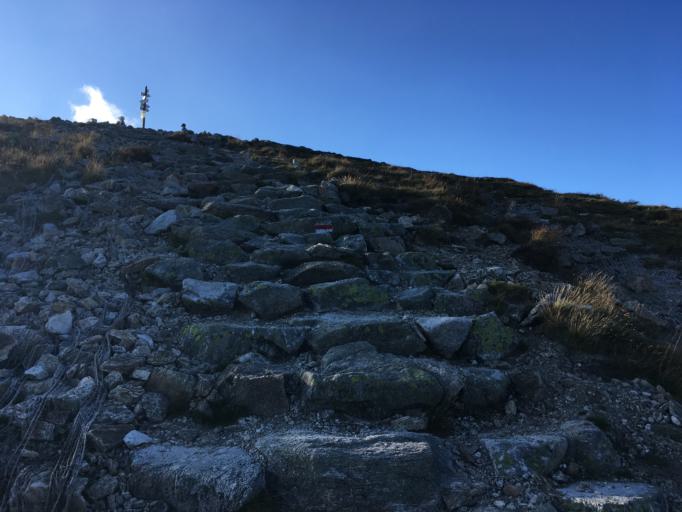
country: PL
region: Lesser Poland Voivodeship
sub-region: Powiat tatrzanski
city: Zakopane
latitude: 49.2363
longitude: 19.9325
